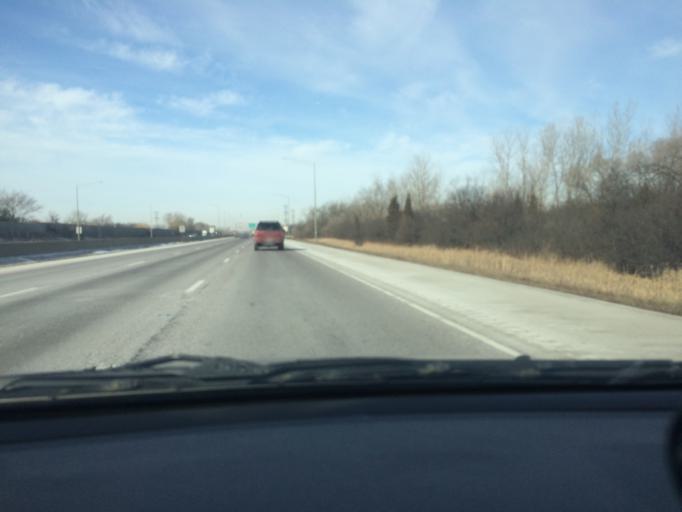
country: US
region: Illinois
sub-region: DuPage County
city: Itasca
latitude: 41.9509
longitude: -88.0075
